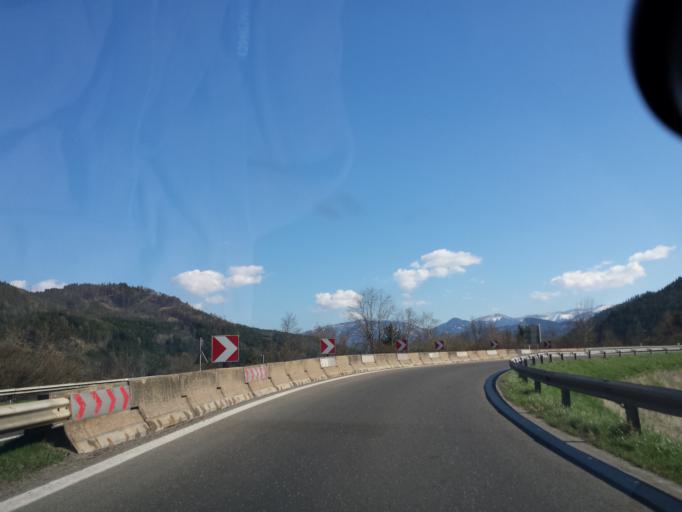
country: AT
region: Styria
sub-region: Politischer Bezirk Leoben
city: Traboch
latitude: 47.3724
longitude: 14.9940
